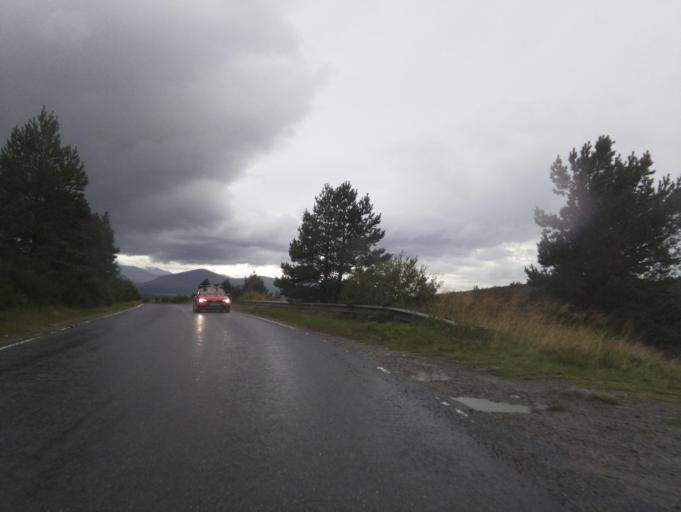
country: GB
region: Scotland
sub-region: Highland
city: Grantown on Spey
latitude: 57.2807
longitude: -3.5588
